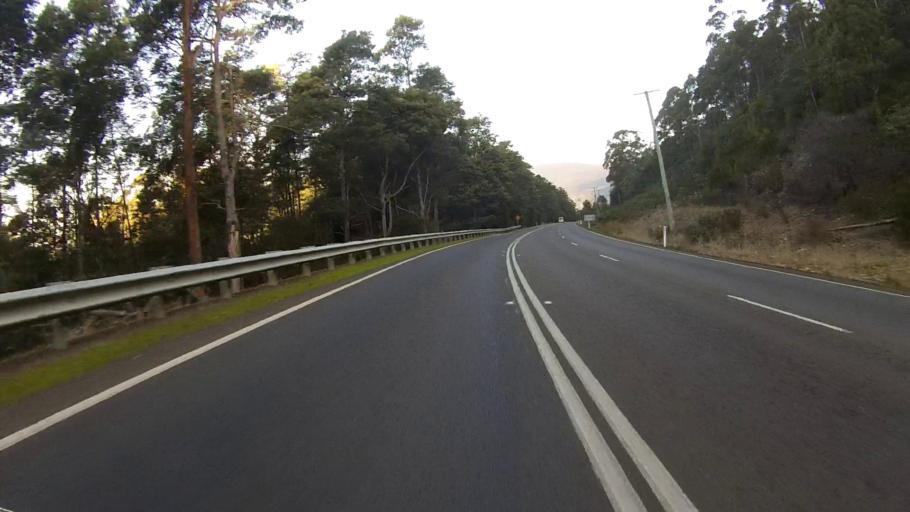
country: AU
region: Tasmania
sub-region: Sorell
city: Sorell
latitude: -42.9978
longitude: 147.9264
